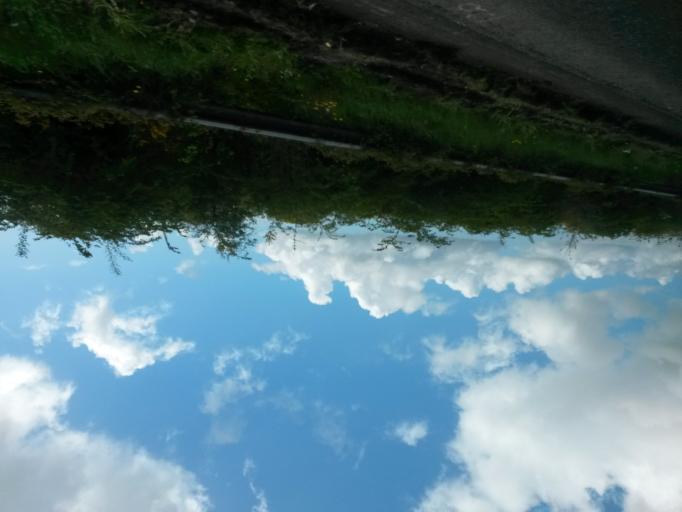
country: IE
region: Leinster
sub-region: Loch Garman
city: Castlebridge
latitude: 52.3808
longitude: -6.5193
